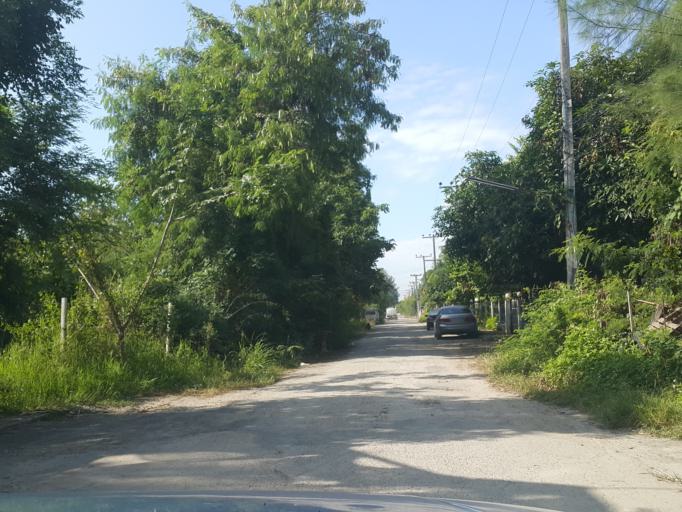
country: TH
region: Chiang Mai
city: Saraphi
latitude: 18.7639
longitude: 99.0643
